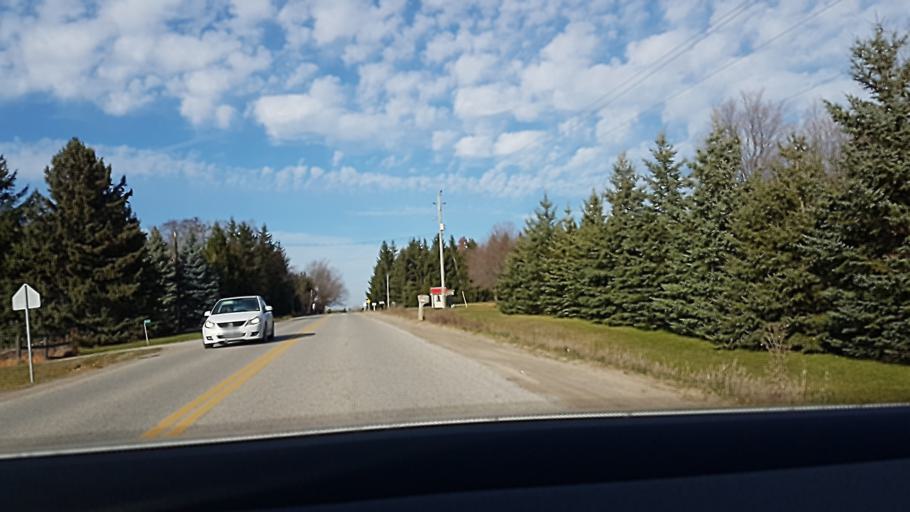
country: CA
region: Ontario
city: Bradford West Gwillimbury
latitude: 44.0444
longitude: -79.7731
